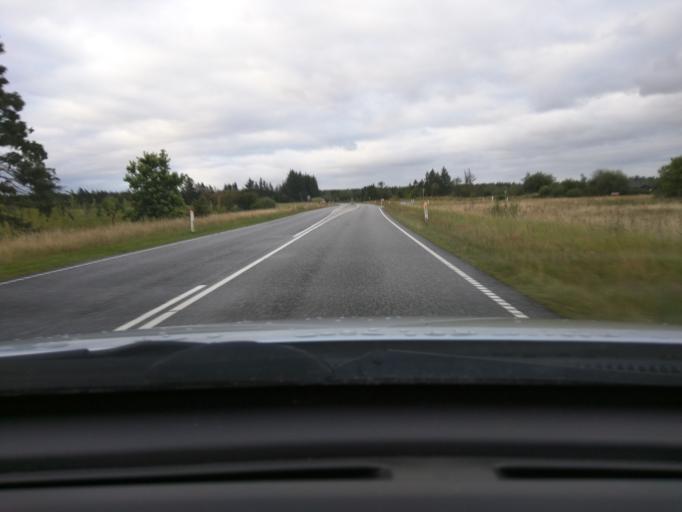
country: DK
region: Central Jutland
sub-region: Ikast-Brande Kommune
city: Bording Kirkeby
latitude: 56.2286
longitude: 9.3209
